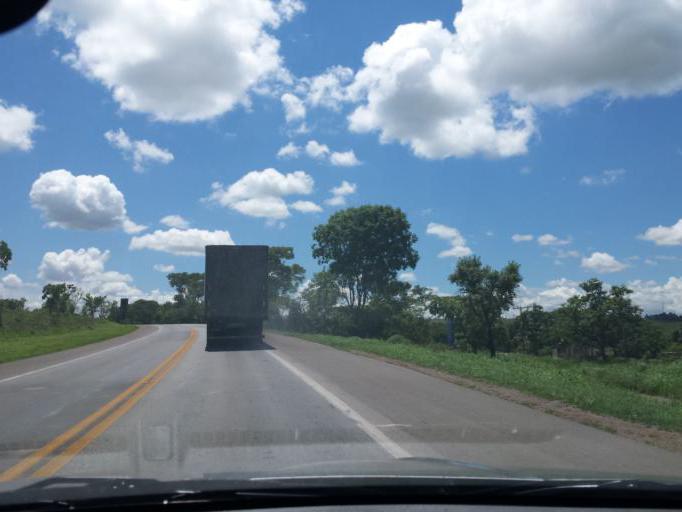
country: BR
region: Goias
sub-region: Cristalina
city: Cristalina
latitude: -16.5407
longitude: -47.7964
